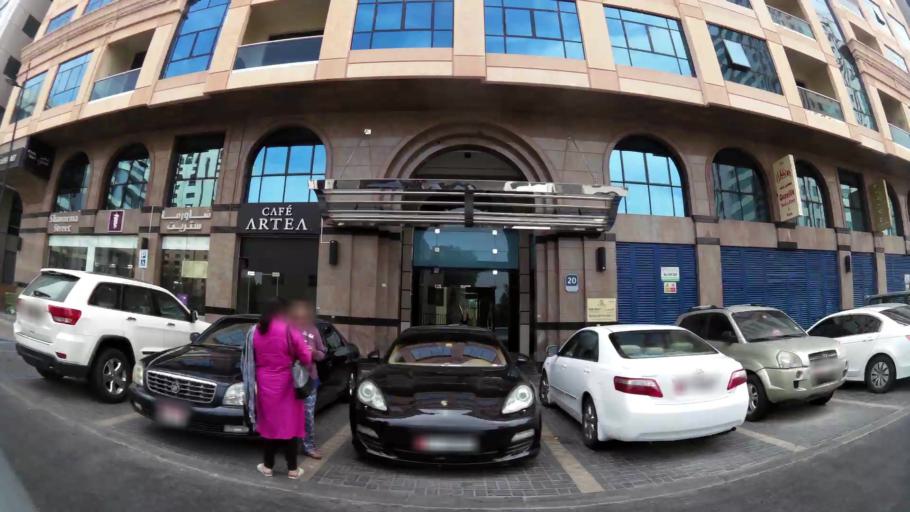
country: AE
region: Abu Dhabi
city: Abu Dhabi
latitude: 24.4690
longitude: 54.3394
